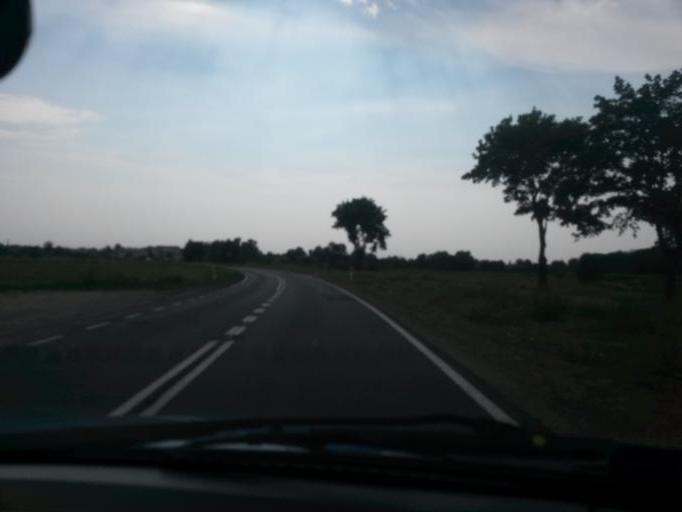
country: PL
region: Masovian Voivodeship
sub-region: Powiat zurominski
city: Biezun
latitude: 52.9667
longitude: 19.8966
